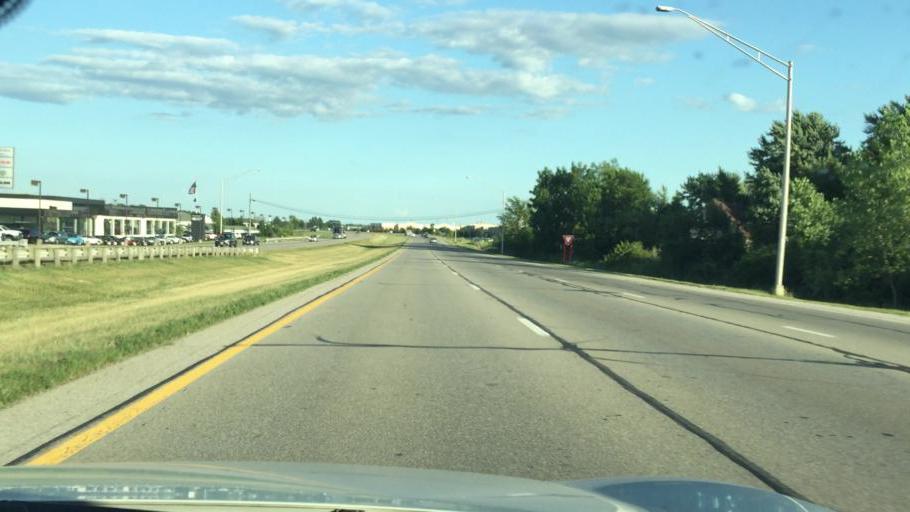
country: US
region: Ohio
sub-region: Union County
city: Marysville
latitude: 40.2363
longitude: -83.3433
